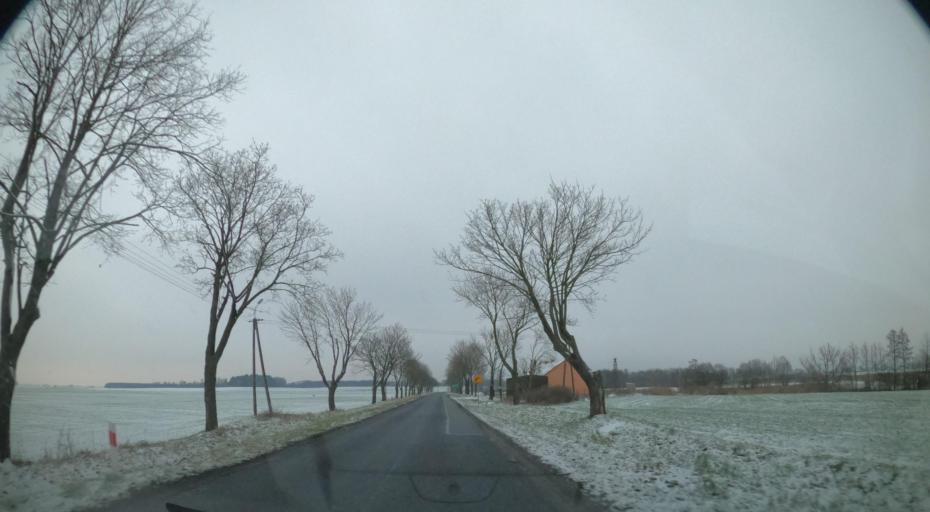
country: PL
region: Kujawsko-Pomorskie
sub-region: Powiat lipnowski
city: Wielgie
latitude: 52.6928
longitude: 19.2792
